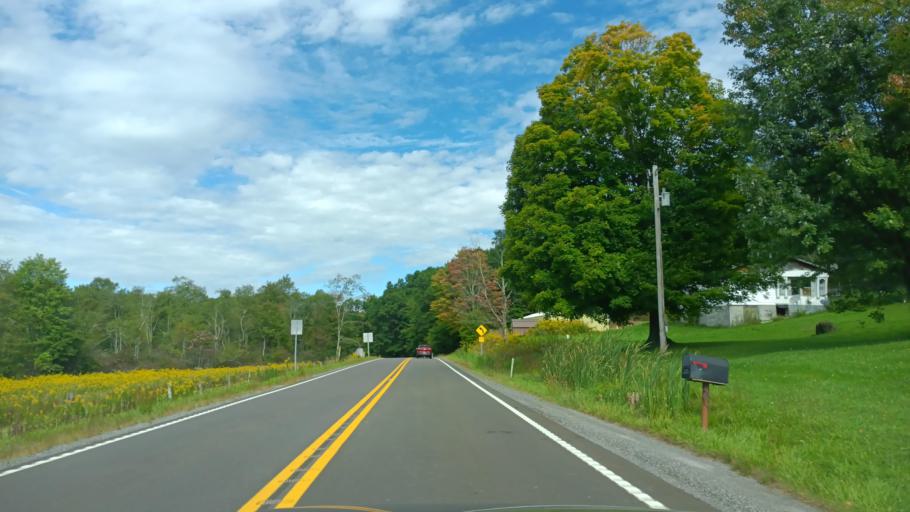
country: US
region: Maryland
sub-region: Garrett County
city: Oakland
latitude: 39.3169
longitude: -79.4854
